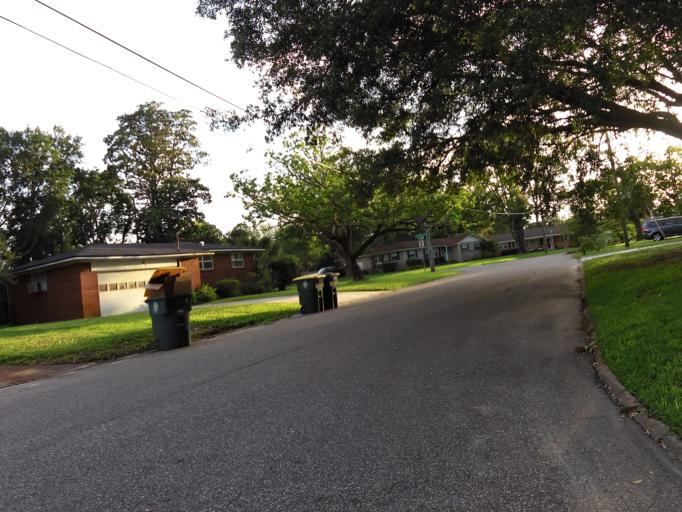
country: US
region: Florida
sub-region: Clay County
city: Orange Park
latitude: 30.2265
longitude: -81.6073
